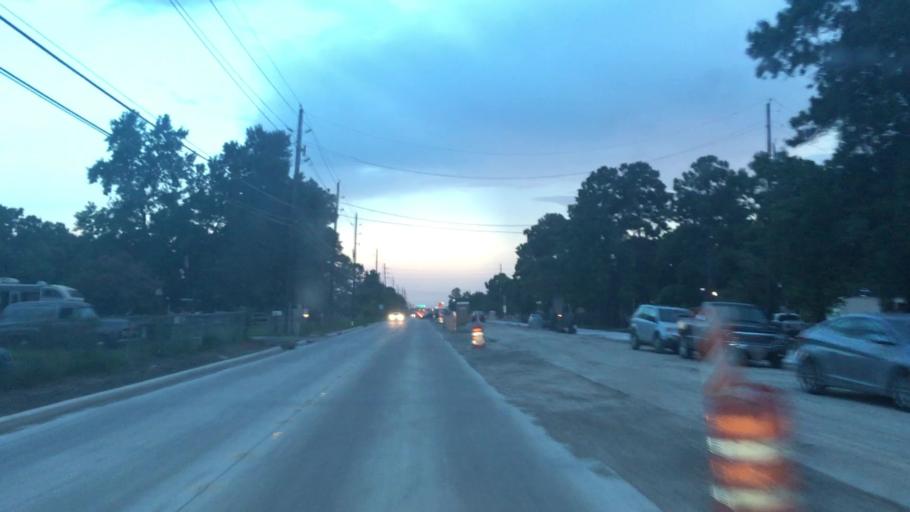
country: US
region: Texas
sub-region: Harris County
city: Humble
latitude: 29.9486
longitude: -95.2497
